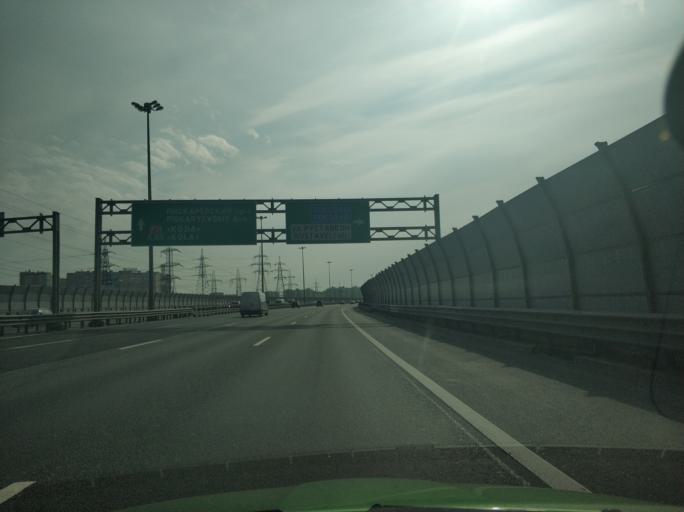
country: RU
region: Leningrad
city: Murino
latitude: 60.0442
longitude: 30.4324
